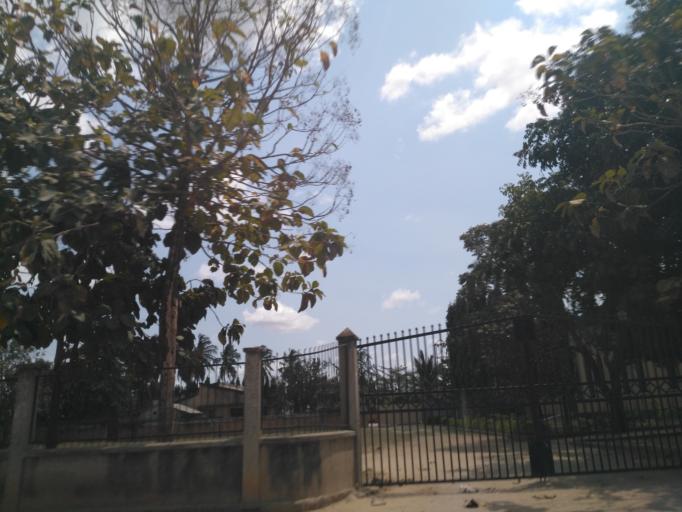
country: TZ
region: Dar es Salaam
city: Dar es Salaam
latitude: -6.8233
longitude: 39.3141
